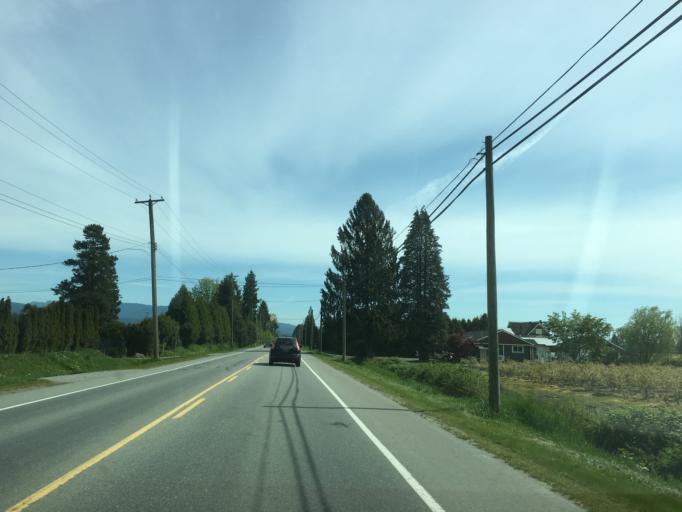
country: CA
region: British Columbia
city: Pitt Meadows
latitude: 49.2442
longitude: -122.6996
